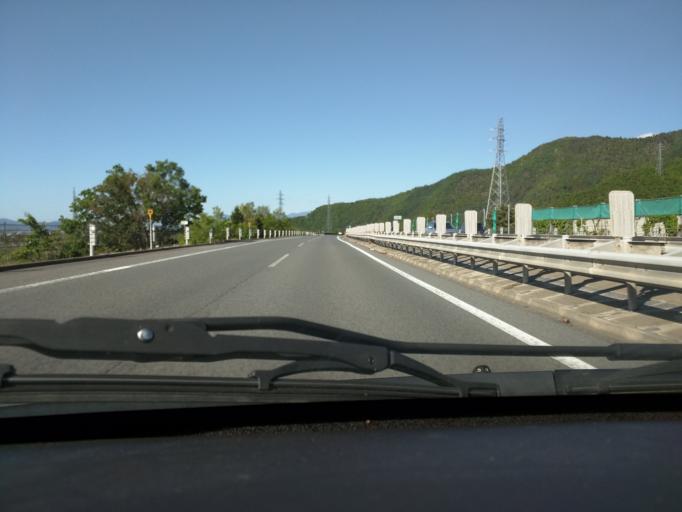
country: JP
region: Nagano
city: Nagano-shi
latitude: 36.6052
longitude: 138.2462
